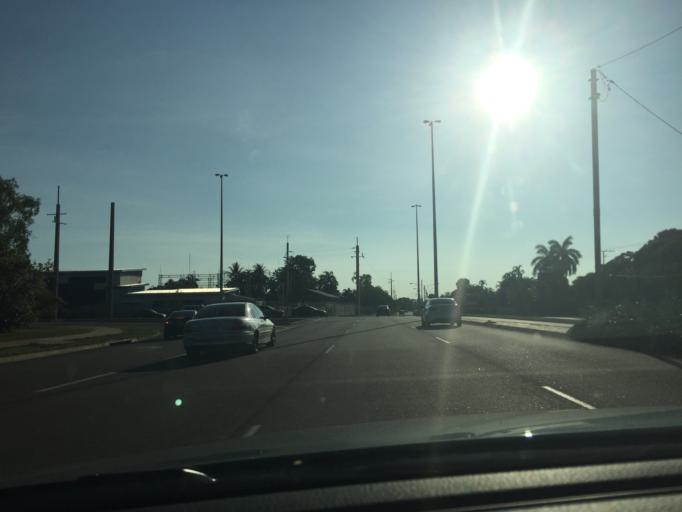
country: AU
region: Northern Territory
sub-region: Darwin
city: Nightcliff
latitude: -12.3826
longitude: 130.8774
